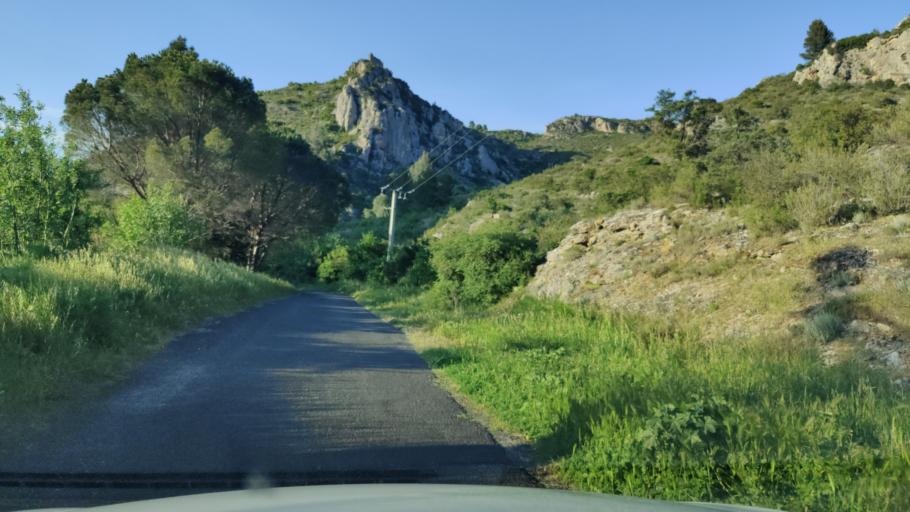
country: FR
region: Languedoc-Roussillon
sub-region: Departement des Pyrenees-Orientales
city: Estagel
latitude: 42.8075
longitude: 2.7447
